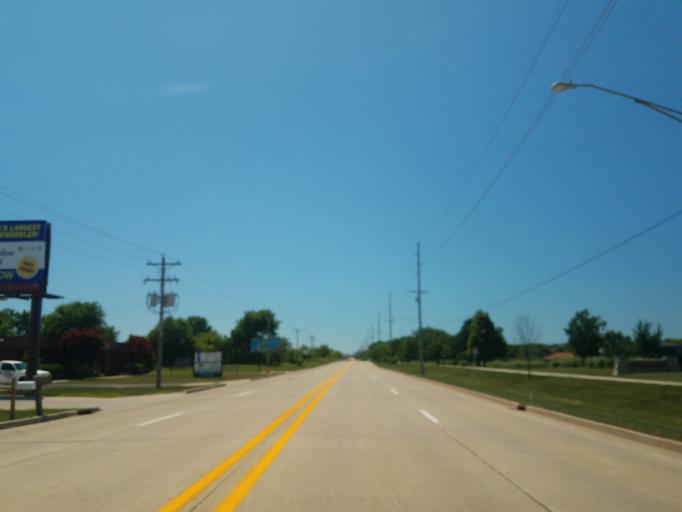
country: US
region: Illinois
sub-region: McLean County
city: Normal
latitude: 40.5027
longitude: -88.9269
